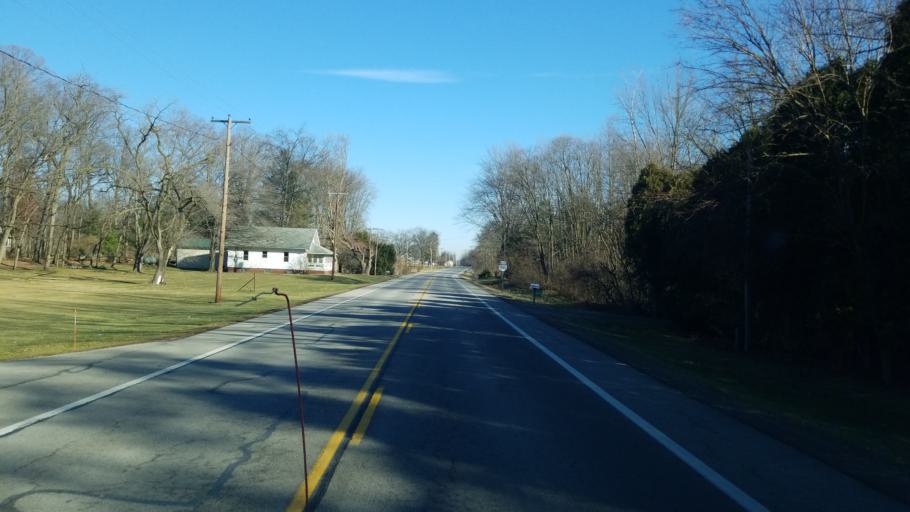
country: US
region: Ohio
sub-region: Wood County
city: Weston
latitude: 41.4292
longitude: -83.8436
